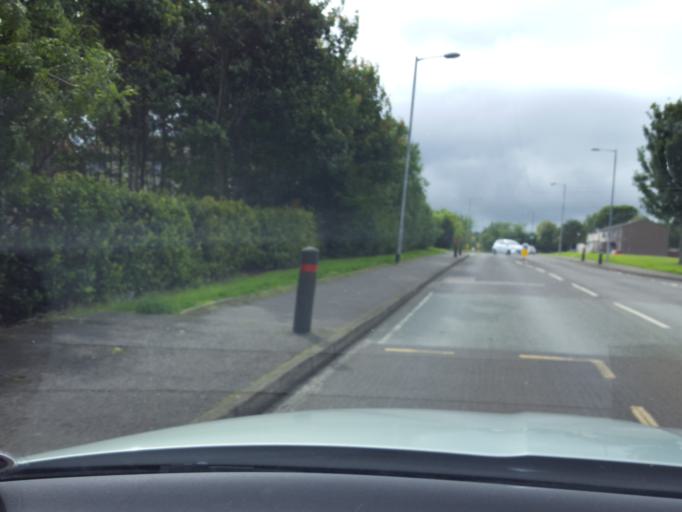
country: GB
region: Scotland
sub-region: Falkirk
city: Bo'ness
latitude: 56.0076
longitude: -3.6003
